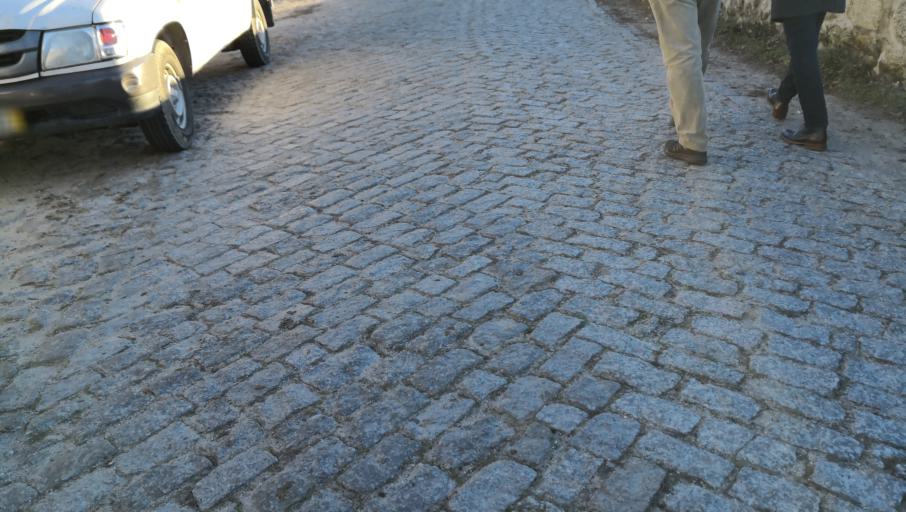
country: PT
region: Vila Real
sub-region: Ribeira de Pena
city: Ribeira de Pena
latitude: 41.5010
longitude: -7.7425
